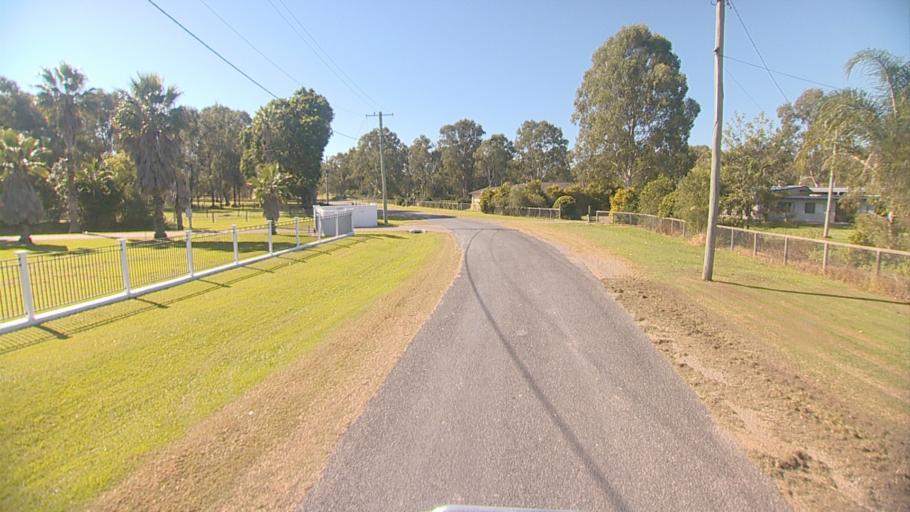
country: AU
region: Queensland
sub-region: Logan
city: Waterford West
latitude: -27.7236
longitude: 153.1248
